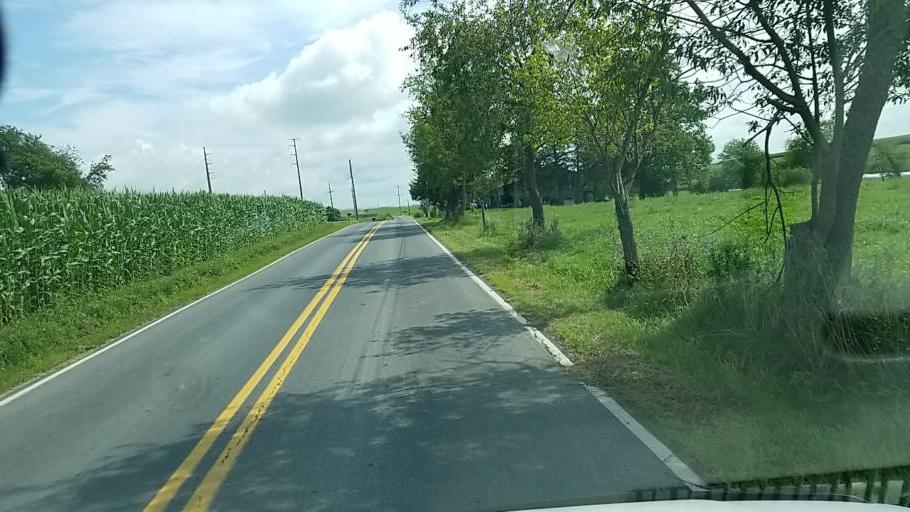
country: US
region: Pennsylvania
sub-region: Dauphin County
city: Millersburg
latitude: 40.5906
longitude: -76.9005
